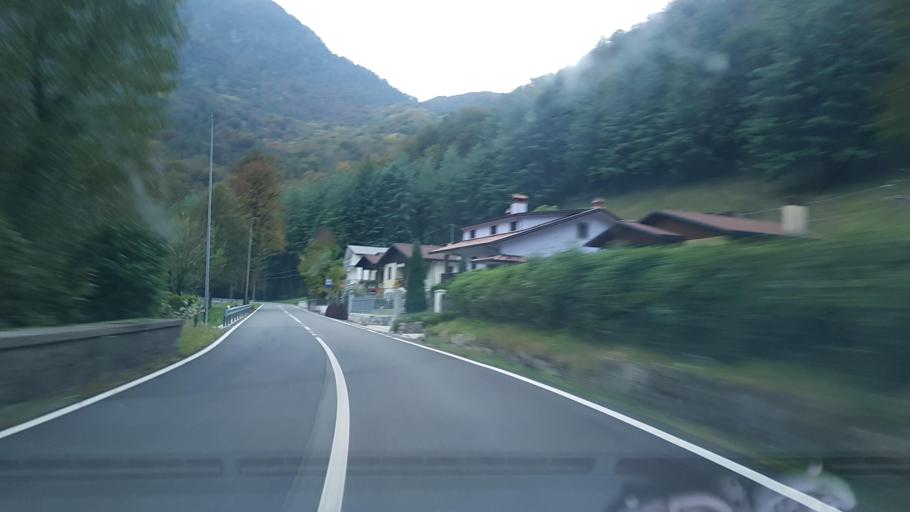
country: IT
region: Friuli Venezia Giulia
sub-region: Provincia di Pordenone
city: Anduins
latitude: 46.2662
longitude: 12.9552
